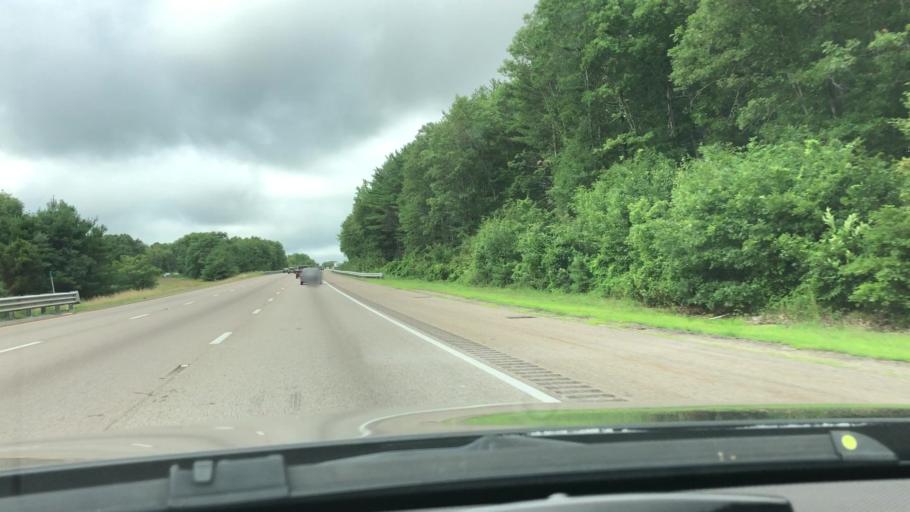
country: US
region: Massachusetts
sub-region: Norfolk County
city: Foxborough
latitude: 42.0685
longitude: -71.2281
